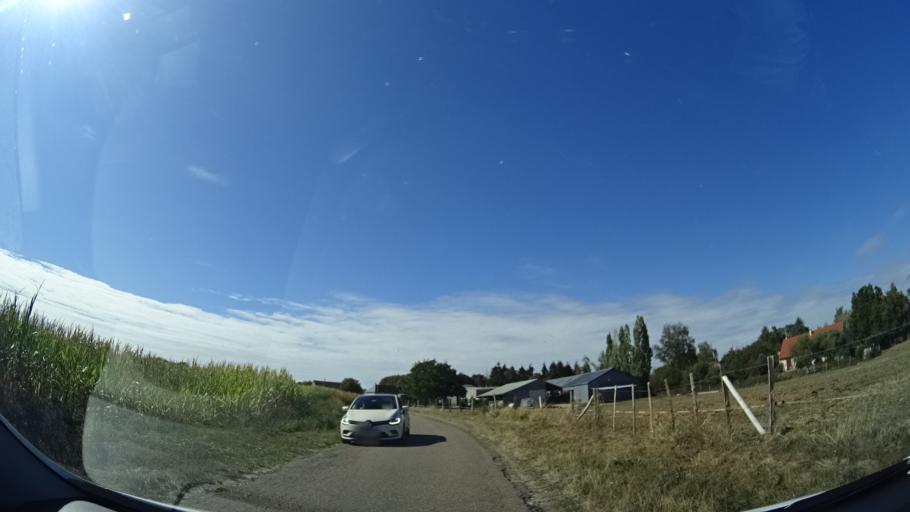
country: FR
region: Centre
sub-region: Departement du Loiret
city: Trigueres
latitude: 47.9574
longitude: 2.9788
